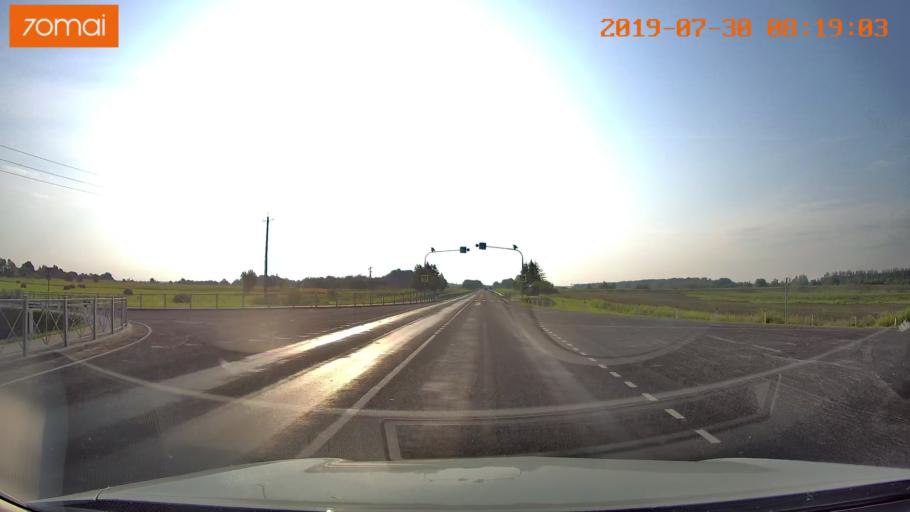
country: RU
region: Kaliningrad
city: Zheleznodorozhnyy
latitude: 54.6301
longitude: 21.4807
